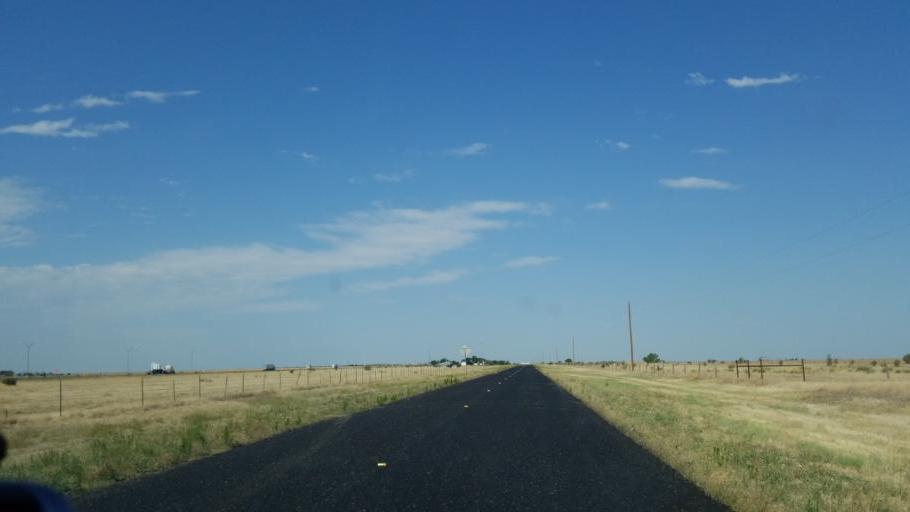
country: US
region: Texas
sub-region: Oldham County
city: Vega
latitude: 35.2644
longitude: -102.7464
